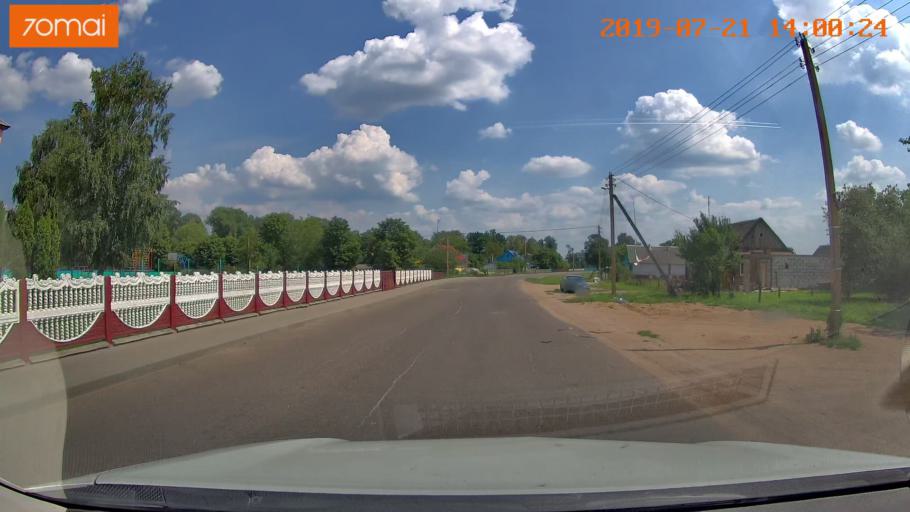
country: BY
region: Grodnenskaya
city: Lyubcha
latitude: 53.7504
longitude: 26.0643
